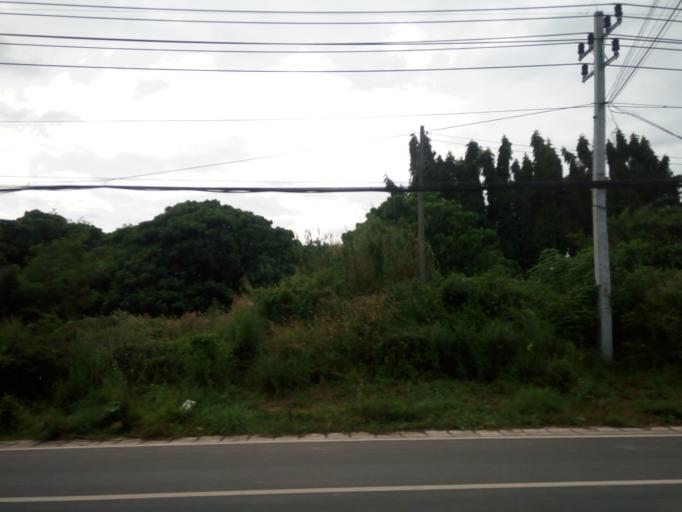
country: TH
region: Phuket
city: Mueang Phuket
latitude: 7.8501
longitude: 98.3817
